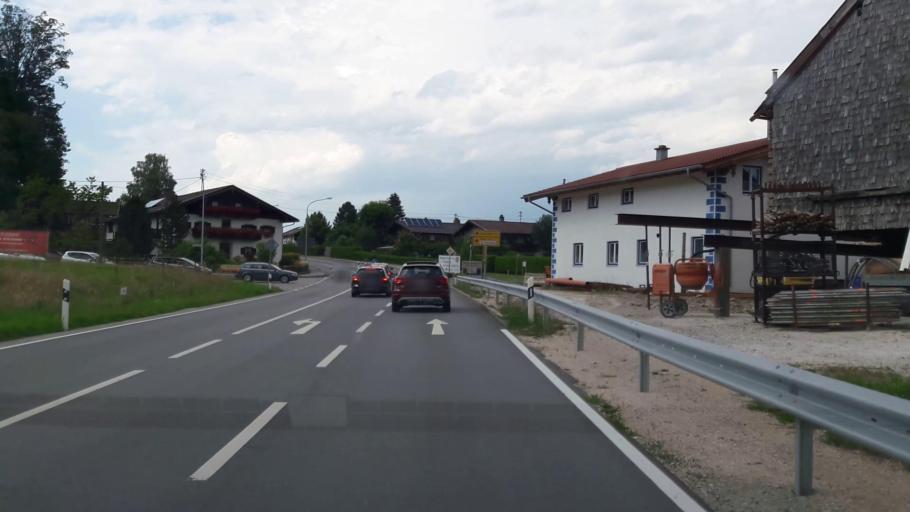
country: DE
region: Bavaria
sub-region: Upper Bavaria
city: Anger
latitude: 47.7996
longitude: 12.8661
